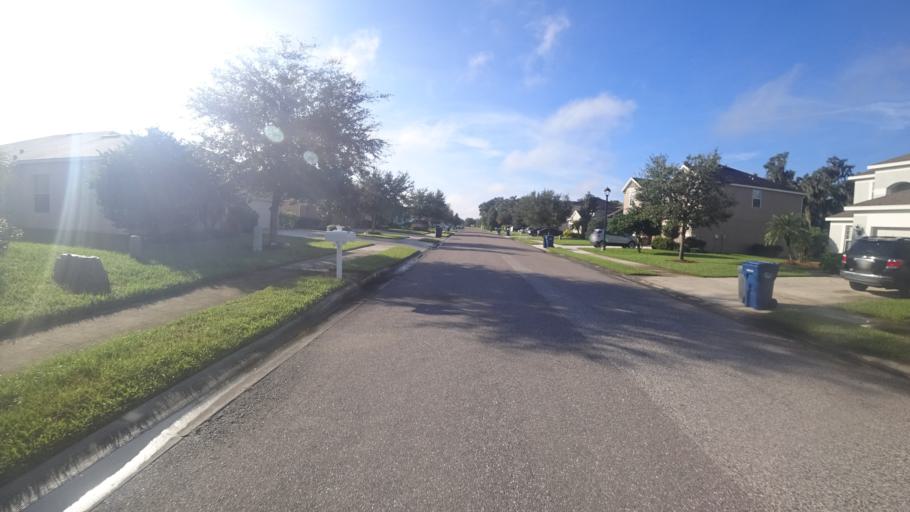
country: US
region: Florida
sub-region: Manatee County
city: Ellenton
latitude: 27.5633
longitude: -82.4659
